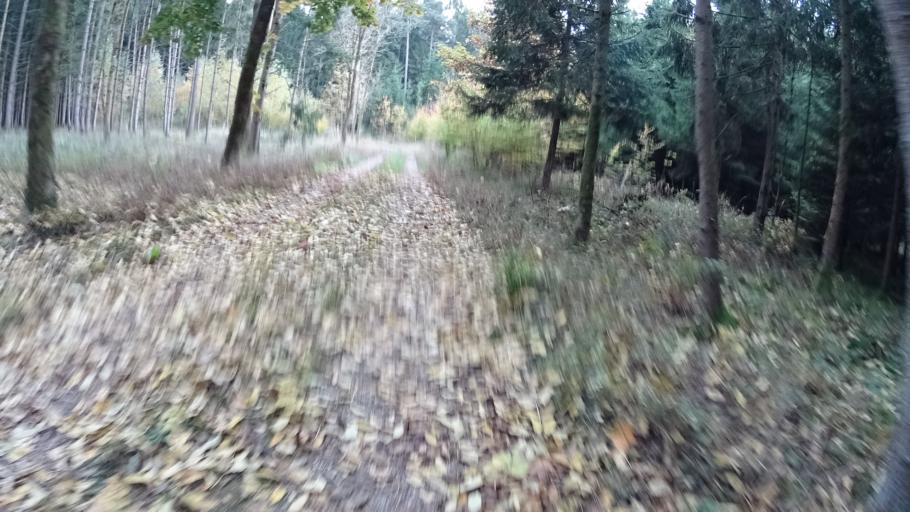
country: DE
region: Bavaria
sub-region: Upper Bavaria
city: Hitzhofen
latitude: 48.8431
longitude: 11.2953
